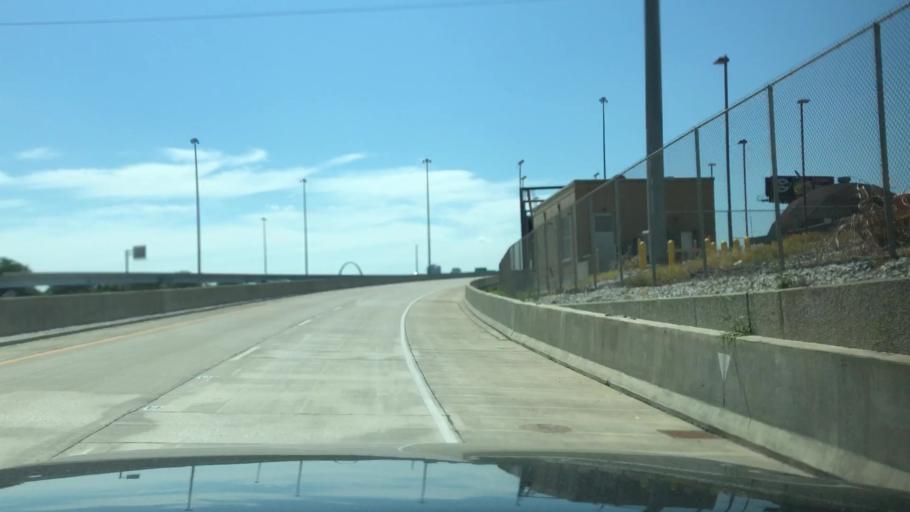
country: US
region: Illinois
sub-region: Saint Clair County
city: East Saint Louis
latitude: 38.6343
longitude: -90.1415
